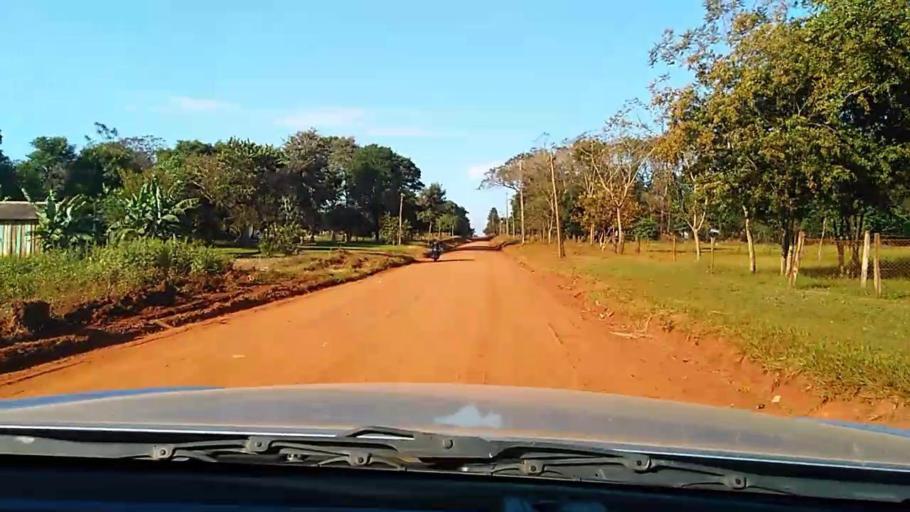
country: PY
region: Alto Parana
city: Doctor Juan Leon Mallorquin
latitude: -25.6877
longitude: -55.3770
